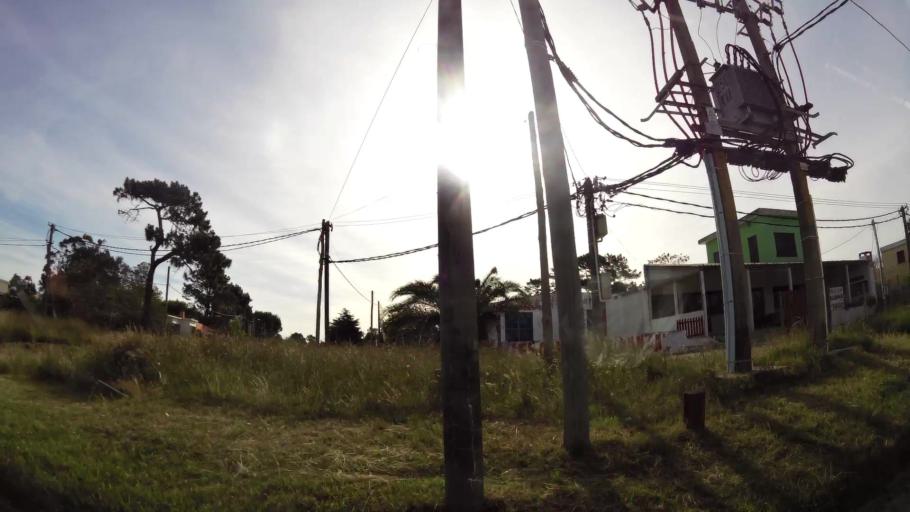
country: UY
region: Canelones
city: Atlantida
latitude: -34.7820
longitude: -55.8386
